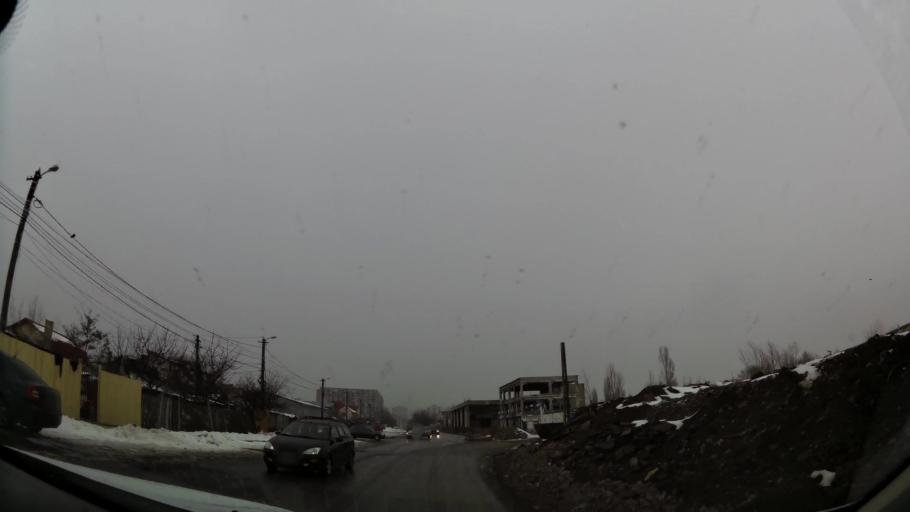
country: RO
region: Ilfov
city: Dobroesti
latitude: 44.4213
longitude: 26.1878
